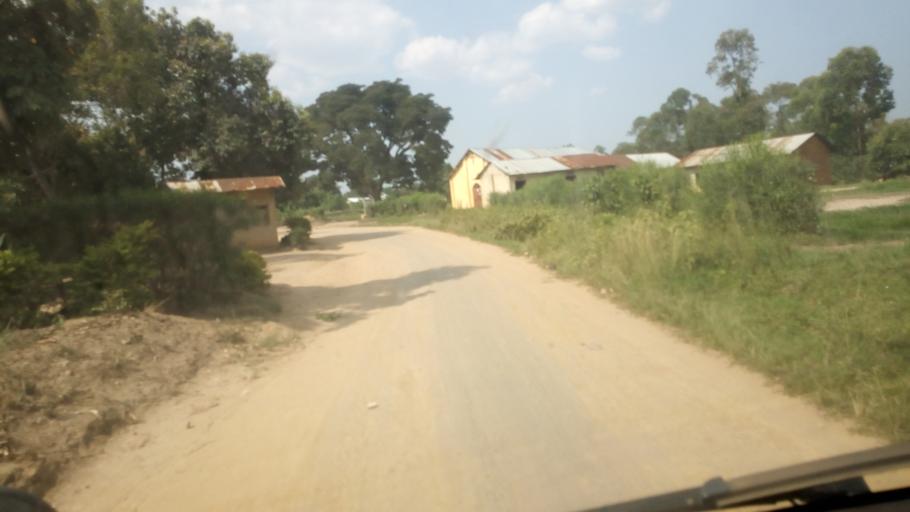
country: UG
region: Western Region
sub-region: Kanungu District
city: Ntungamo
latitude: -0.7892
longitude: 29.6871
